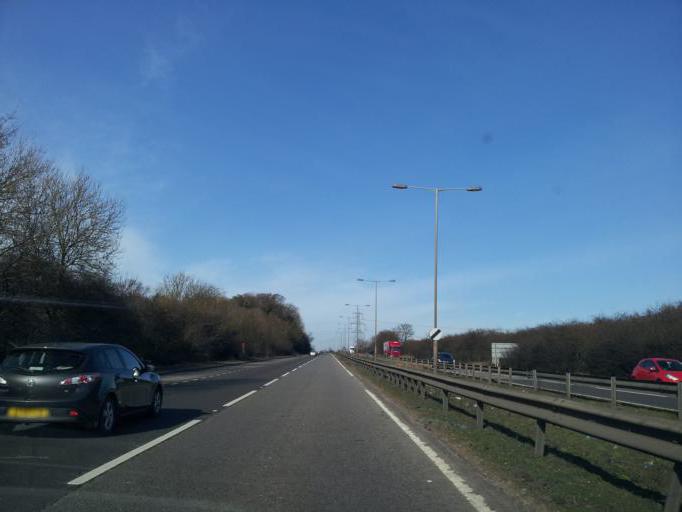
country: GB
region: England
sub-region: Lincolnshire
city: Grantham
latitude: 52.8654
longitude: -0.6297
